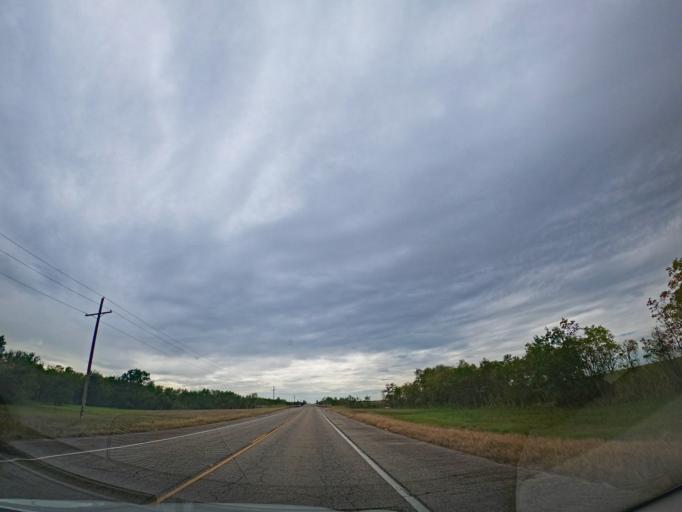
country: US
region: Mississippi
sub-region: Hancock County
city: Pearlington
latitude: 30.2373
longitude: -89.6272
